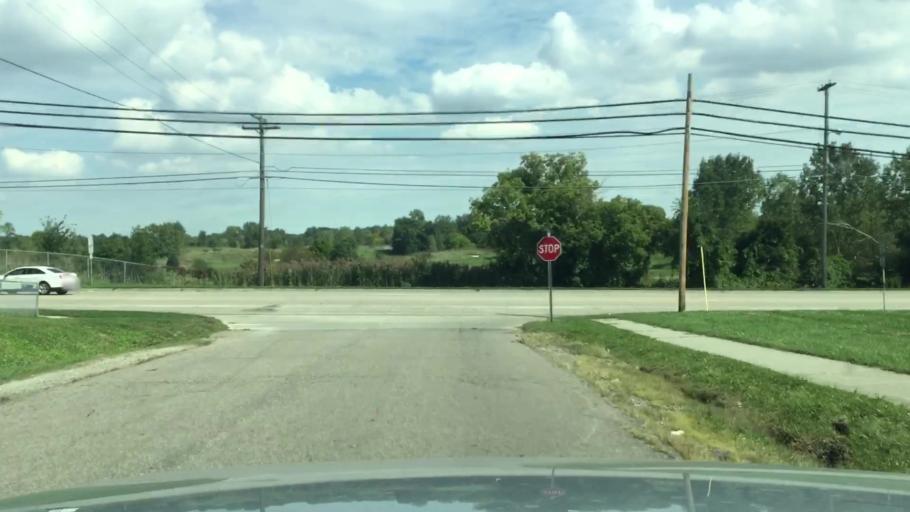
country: US
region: Michigan
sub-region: Wayne County
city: Wayne
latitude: 42.2900
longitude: -83.3496
